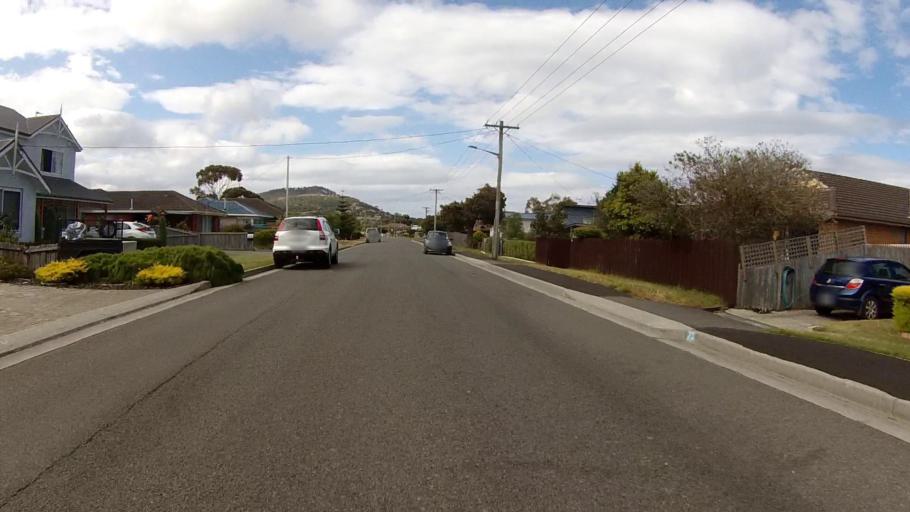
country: AU
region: Tasmania
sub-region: Clarence
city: Lauderdale
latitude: -42.8984
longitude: 147.4948
